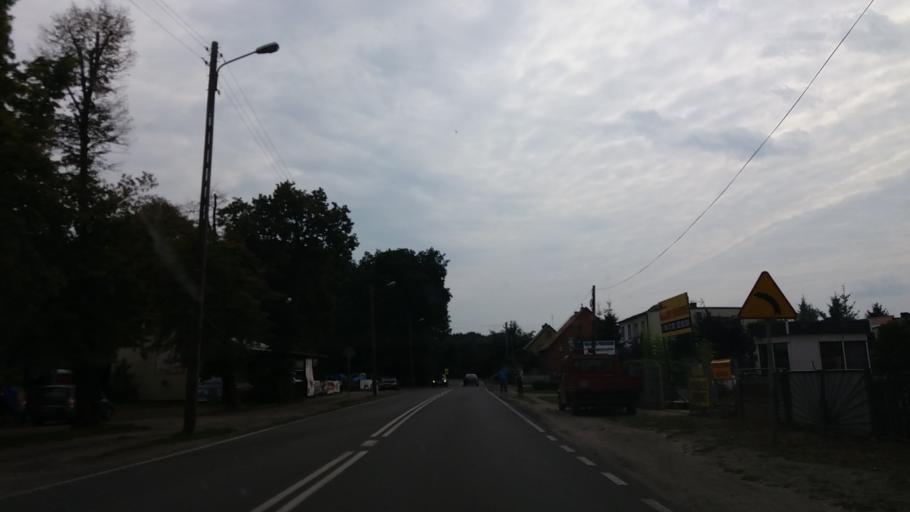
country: PL
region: Lubusz
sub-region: Powiat miedzyrzecki
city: Skwierzyna
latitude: 52.5939
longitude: 15.5080
